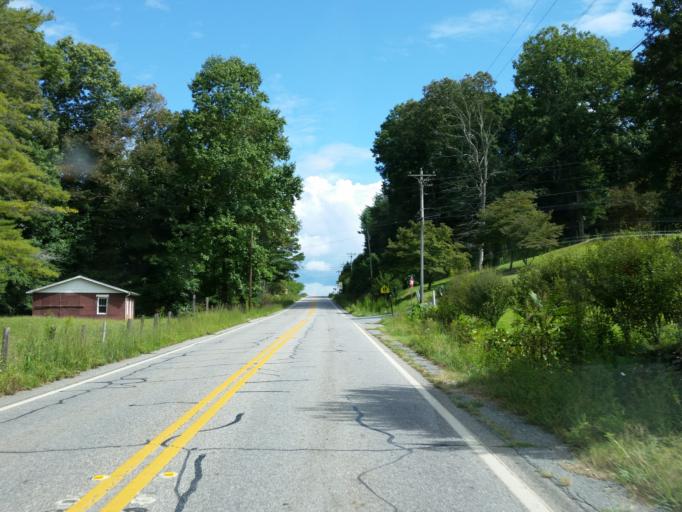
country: US
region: Georgia
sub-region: Fannin County
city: Blue Ridge
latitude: 34.8826
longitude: -84.2518
